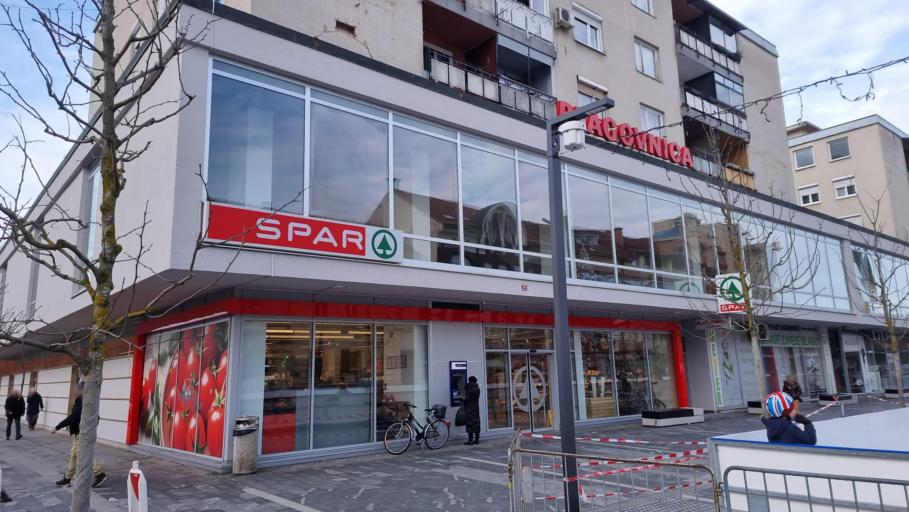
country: SI
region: Murska Sobota
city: Murska Sobota
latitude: 46.6598
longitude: 16.1659
